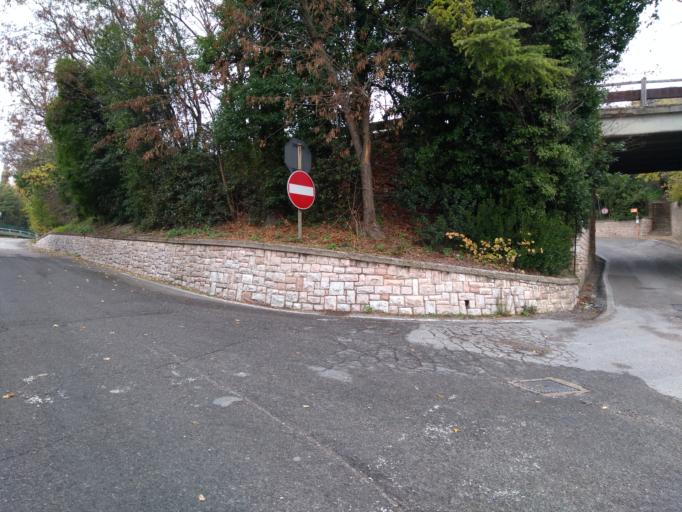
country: IT
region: Umbria
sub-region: Provincia di Perugia
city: Assisi
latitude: 43.0653
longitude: 12.6191
